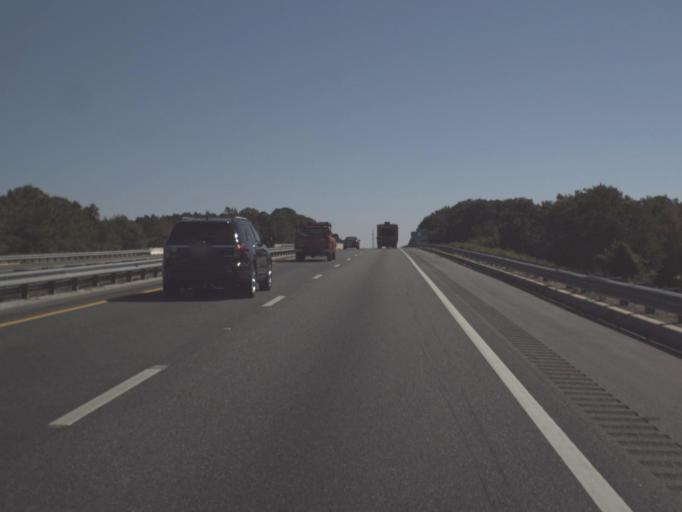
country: US
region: Florida
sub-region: Lake County
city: Montverde
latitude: 28.5595
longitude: -81.6791
